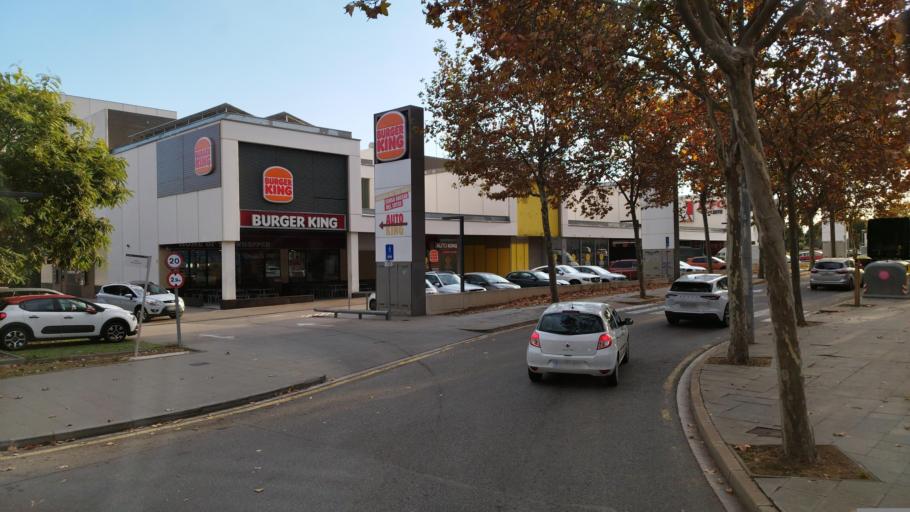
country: ES
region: Catalonia
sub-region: Provincia de Barcelona
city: Castelldefels
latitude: 41.2825
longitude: 1.9890
